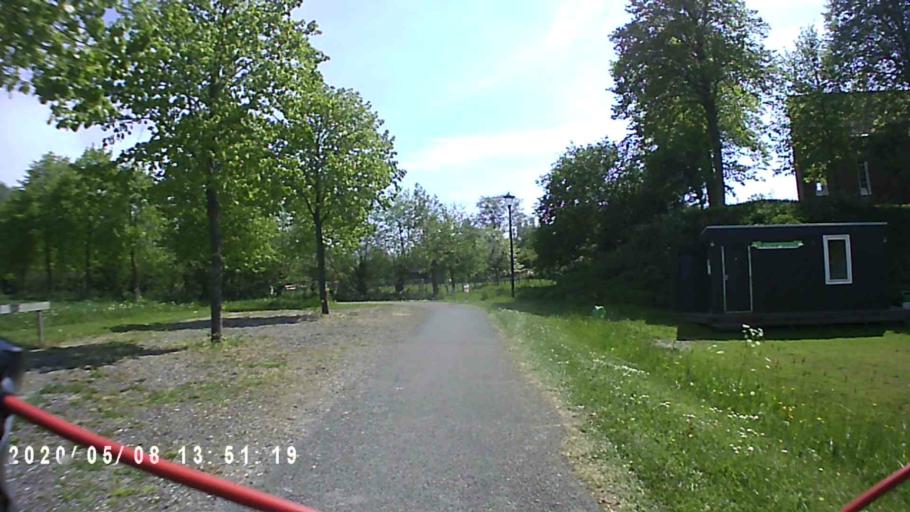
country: NL
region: Groningen
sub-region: Gemeente Appingedam
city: Appingedam
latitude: 53.3401
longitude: 6.7795
